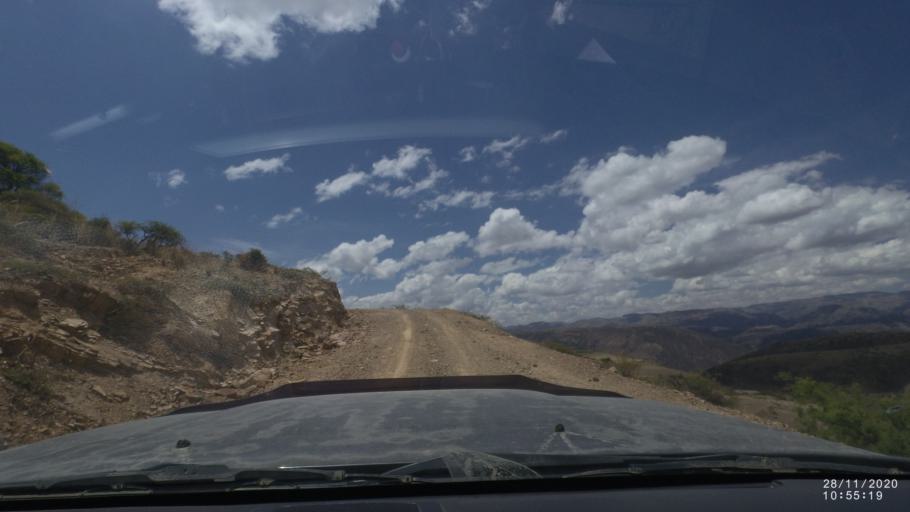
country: BO
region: Cochabamba
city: Capinota
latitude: -17.7757
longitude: -66.1151
